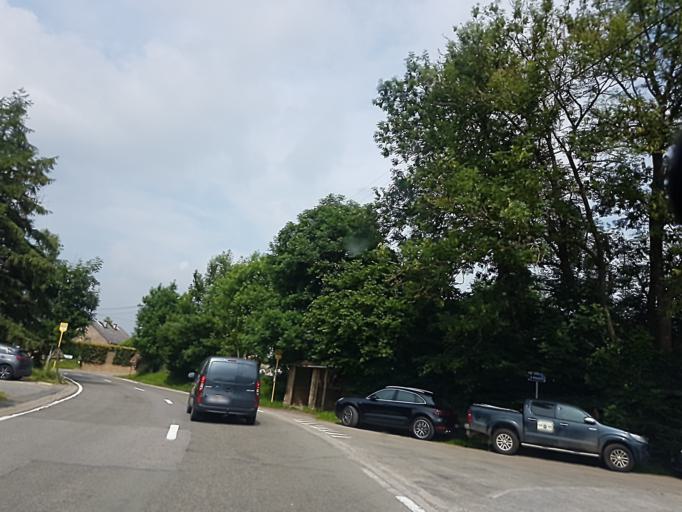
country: BE
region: Wallonia
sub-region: Province du Luxembourg
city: Manhay
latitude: 50.3007
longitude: 5.6979
